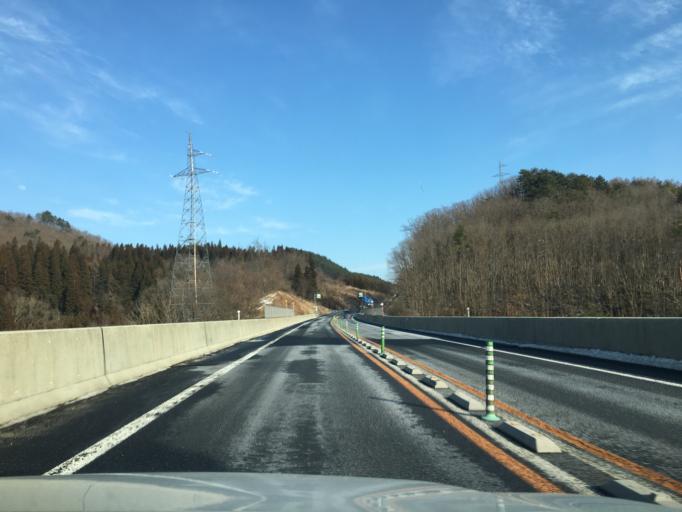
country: JP
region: Yamagata
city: Sagae
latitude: 38.4358
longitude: 140.1379
